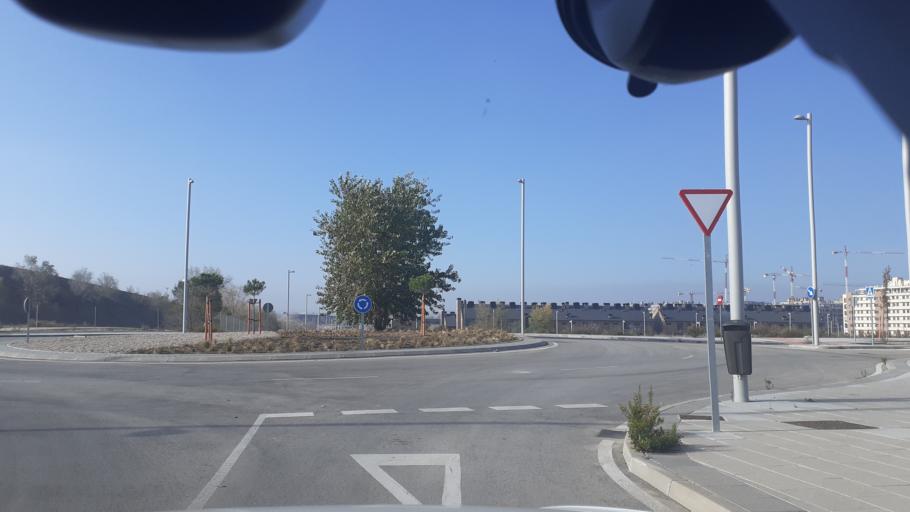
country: ES
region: Madrid
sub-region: Provincia de Madrid
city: Coslada
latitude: 40.3980
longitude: -3.5614
